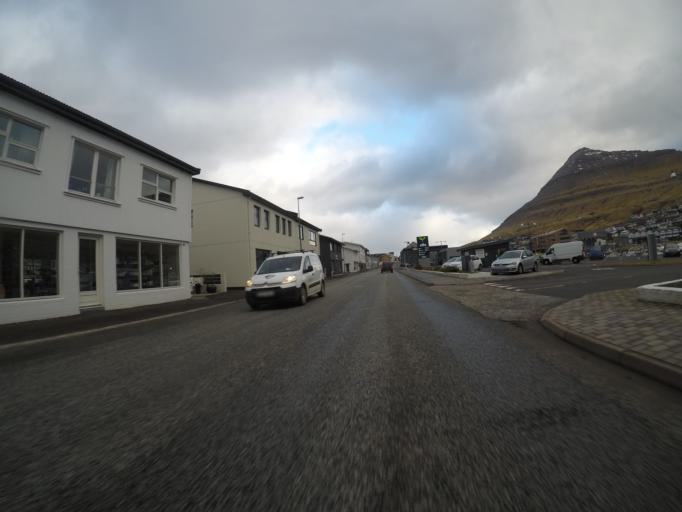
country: FO
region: Nordoyar
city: Klaksvik
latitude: 62.2296
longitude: -6.5867
